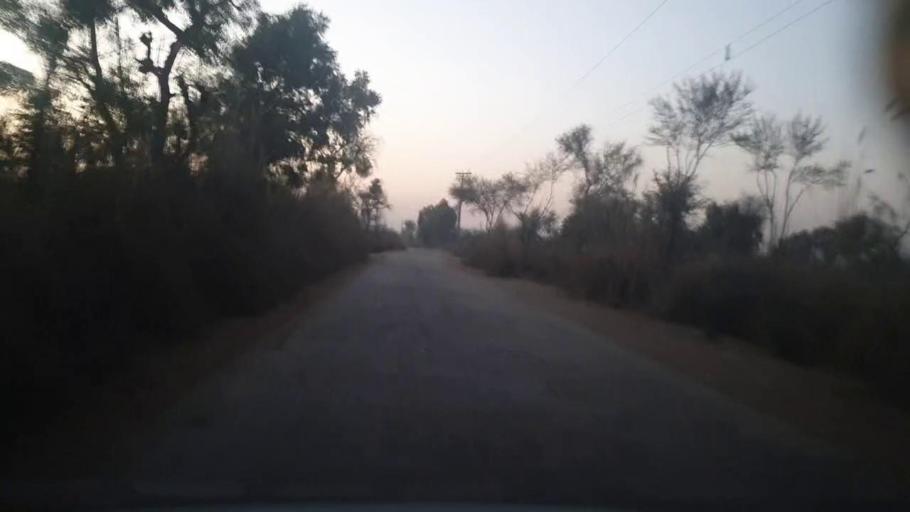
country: PK
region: Sindh
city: Kandiari
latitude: 26.6832
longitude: 68.9383
